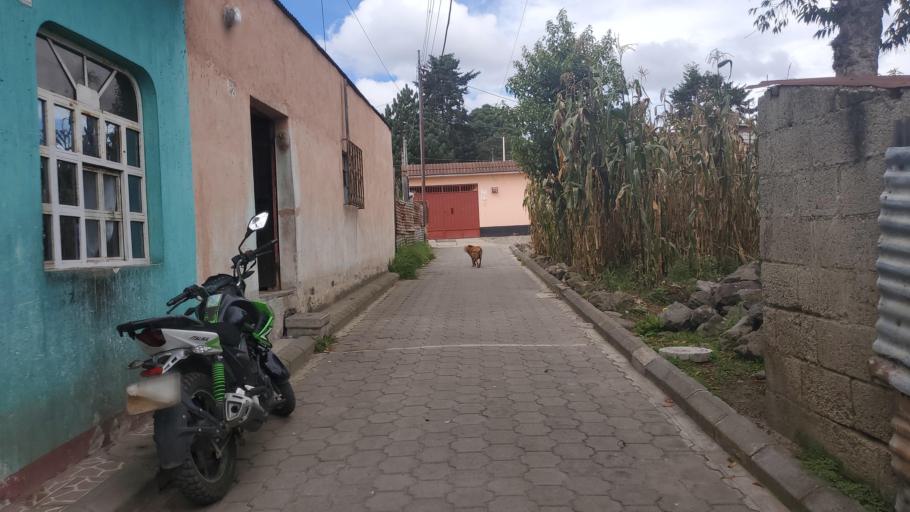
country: GT
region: Quetzaltenango
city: Quetzaltenango
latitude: 14.8343
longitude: -91.5373
